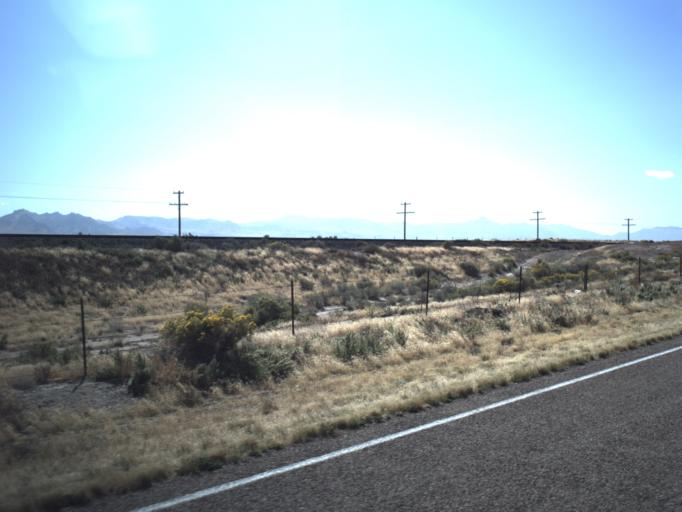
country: US
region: Utah
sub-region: Beaver County
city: Milford
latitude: 38.6673
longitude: -112.9809
